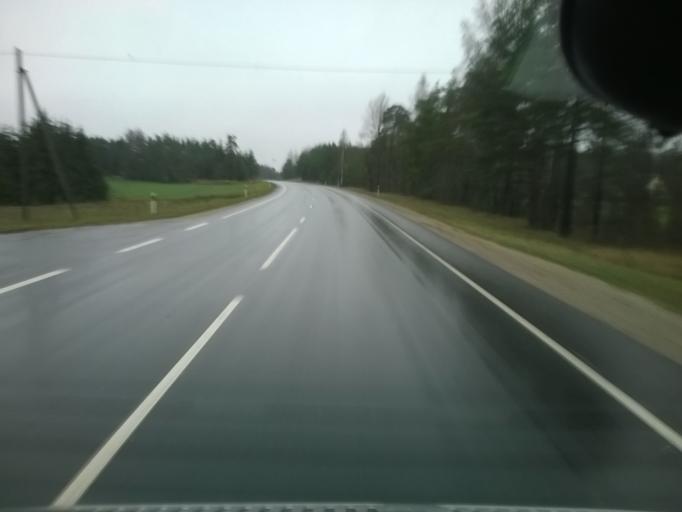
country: EE
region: Harju
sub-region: Nissi vald
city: Turba
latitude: 59.1003
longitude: 24.2525
